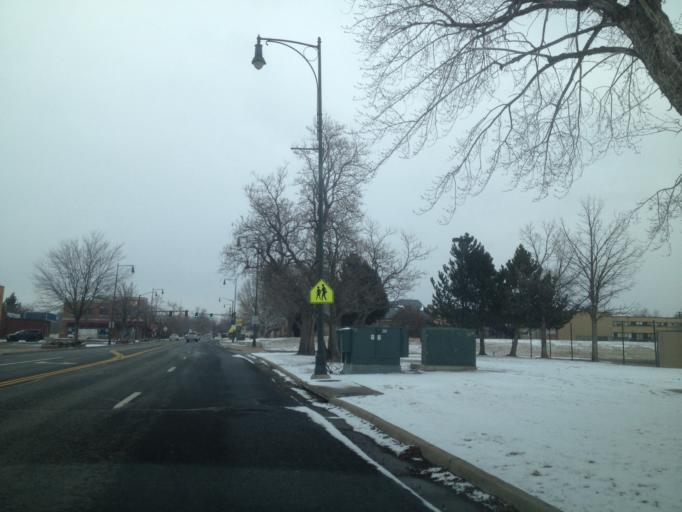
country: US
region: Colorado
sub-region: Adams County
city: Westminster
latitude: 39.8284
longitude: -105.0343
